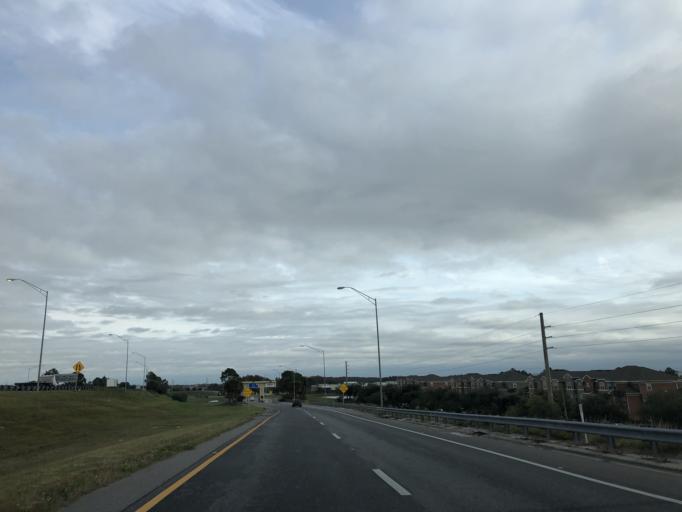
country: US
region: Florida
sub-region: Orange County
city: Meadow Woods
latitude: 28.3680
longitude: -81.3724
